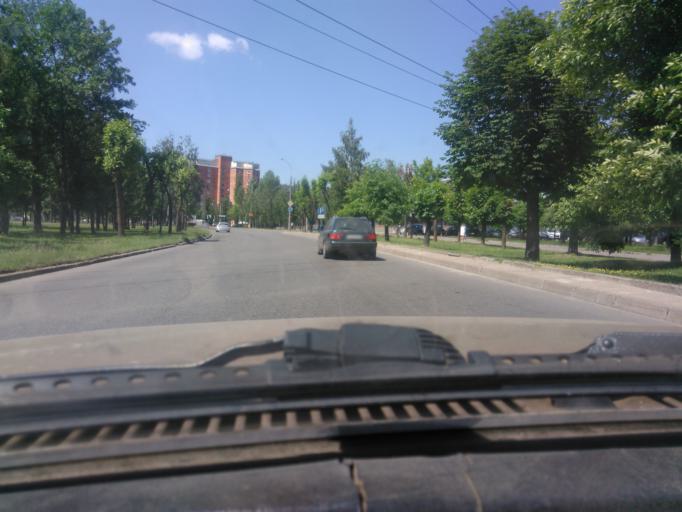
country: BY
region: Mogilev
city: Mahilyow
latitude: 53.9260
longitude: 30.3643
